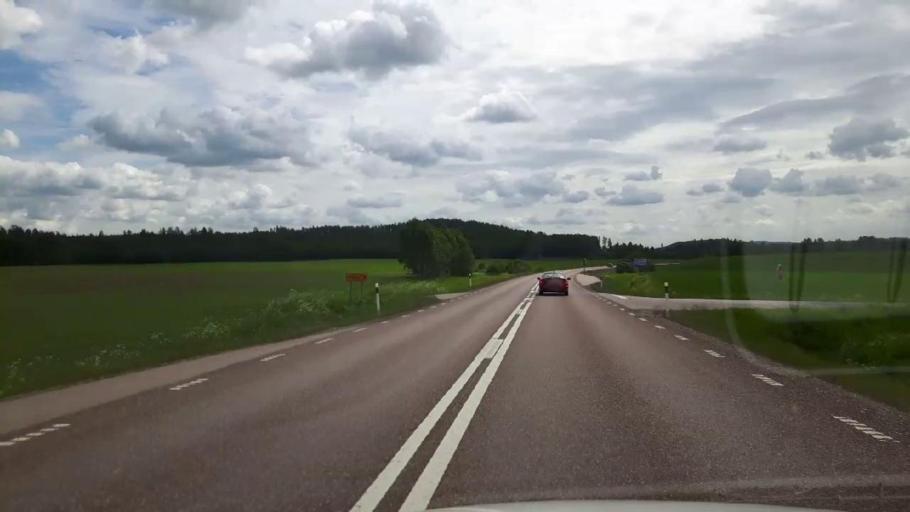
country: SE
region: Dalarna
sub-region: Hedemora Kommun
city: Hedemora
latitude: 60.3322
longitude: 15.9472
